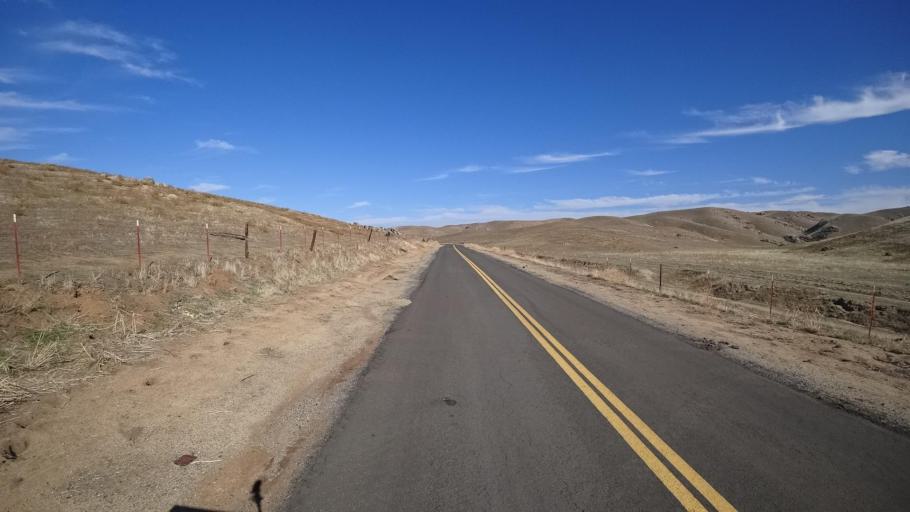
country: US
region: California
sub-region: Tulare County
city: Richgrove
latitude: 35.6759
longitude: -118.8954
